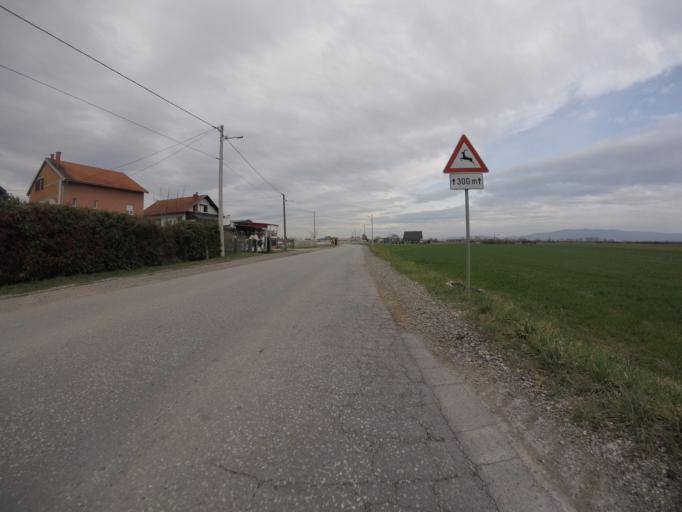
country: HR
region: Zagrebacka
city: Gradici
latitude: 45.7101
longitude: 16.0334
